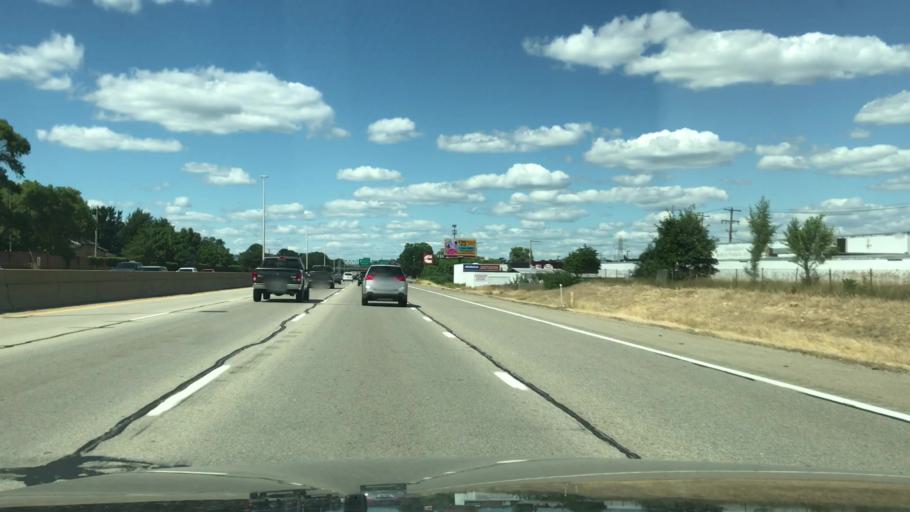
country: US
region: Michigan
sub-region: Kent County
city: Wyoming
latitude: 42.8934
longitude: -85.6783
